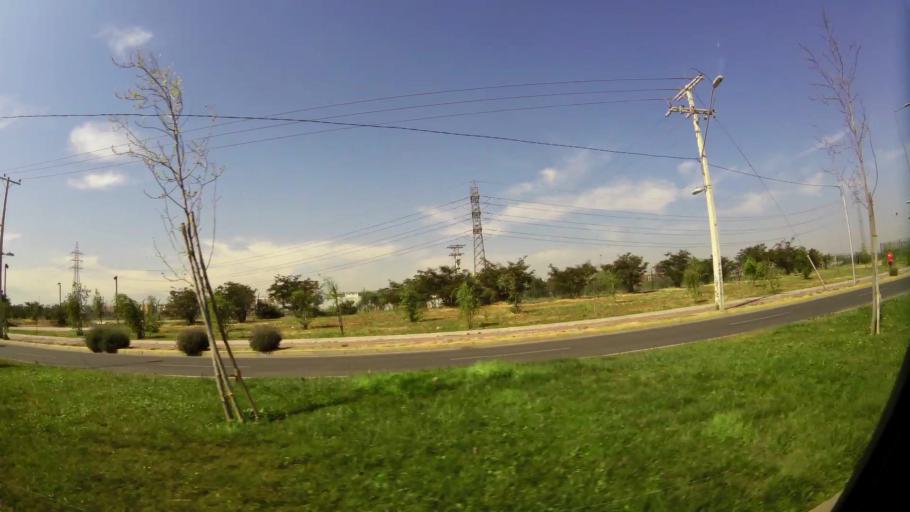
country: CL
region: Santiago Metropolitan
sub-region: Provincia de Santiago
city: Lo Prado
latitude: -33.4830
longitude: -70.7405
